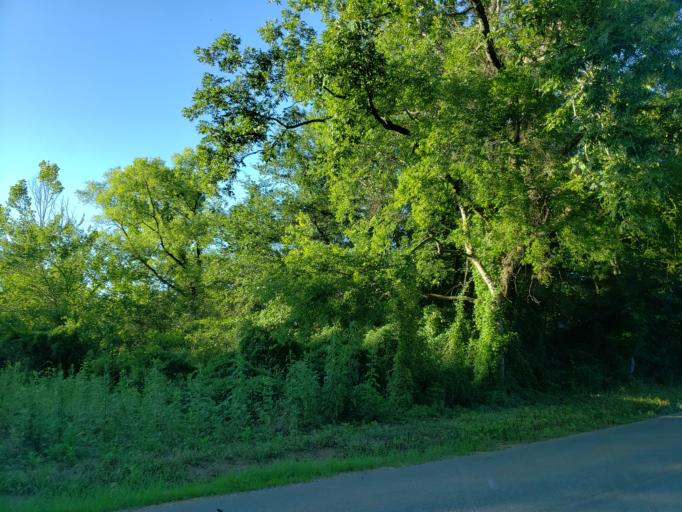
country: US
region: Georgia
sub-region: Polk County
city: Aragon
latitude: 34.0857
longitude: -85.0283
